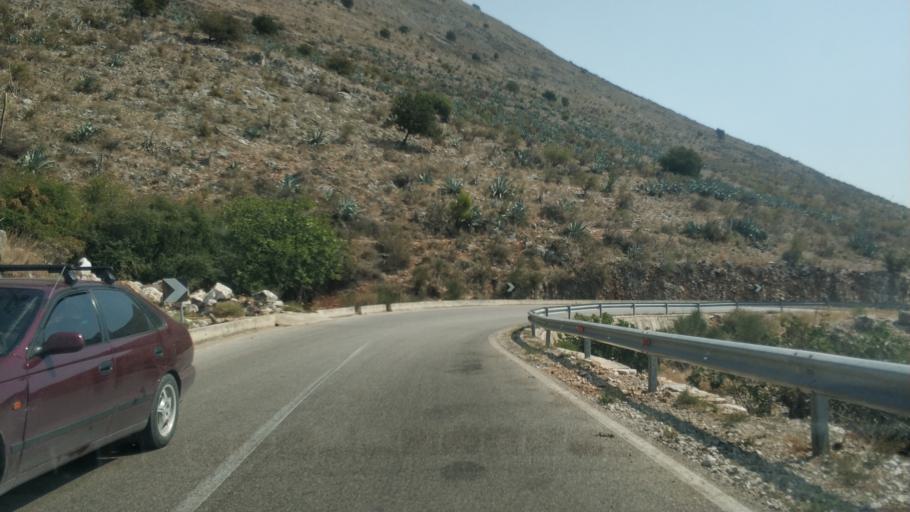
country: AL
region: Vlore
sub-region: Rrethi i Vlores
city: Himare
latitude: 40.0686
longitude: 19.7916
